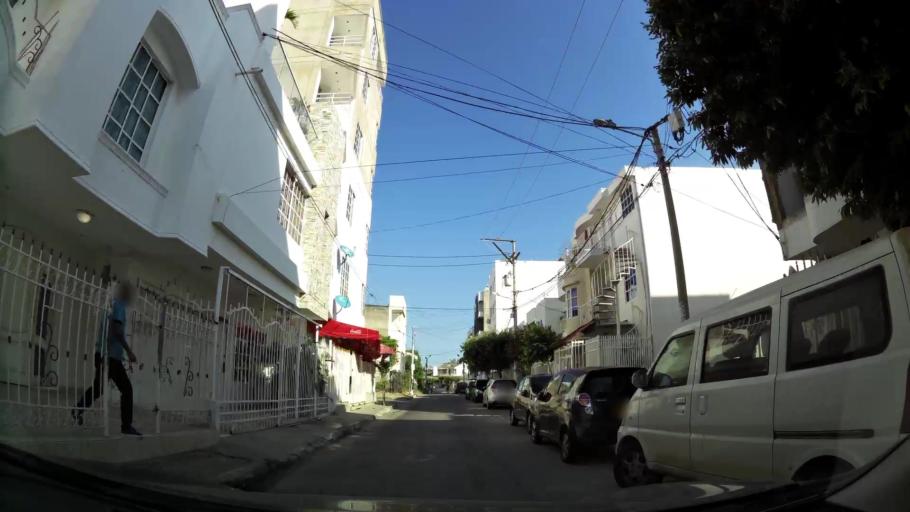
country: CO
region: Bolivar
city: Cartagena
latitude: 10.3914
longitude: -75.4966
